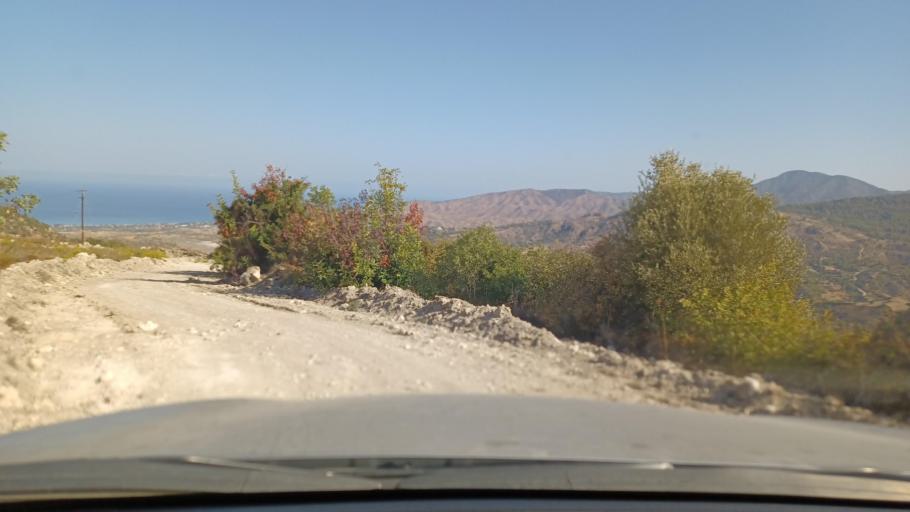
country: CY
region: Pafos
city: Polis
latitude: 35.0110
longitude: 32.4856
